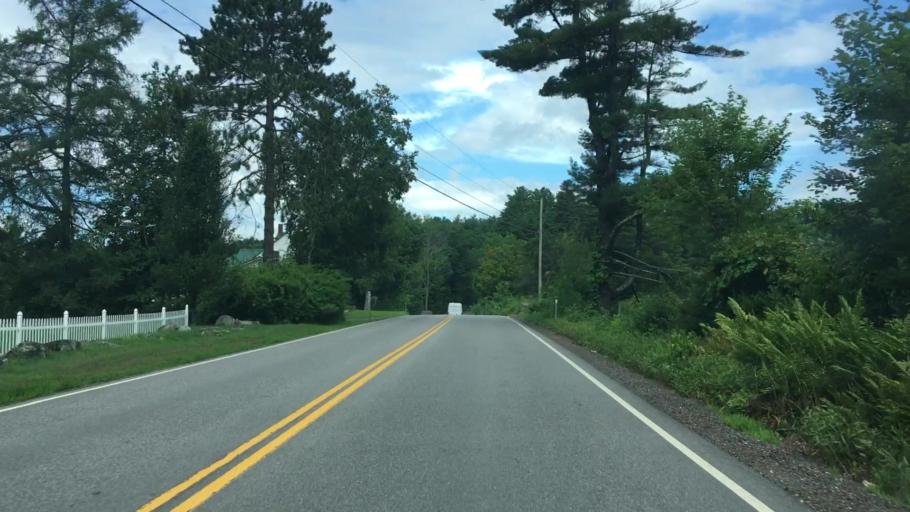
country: US
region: New Hampshire
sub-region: Belknap County
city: Laconia
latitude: 43.5803
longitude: -71.5122
